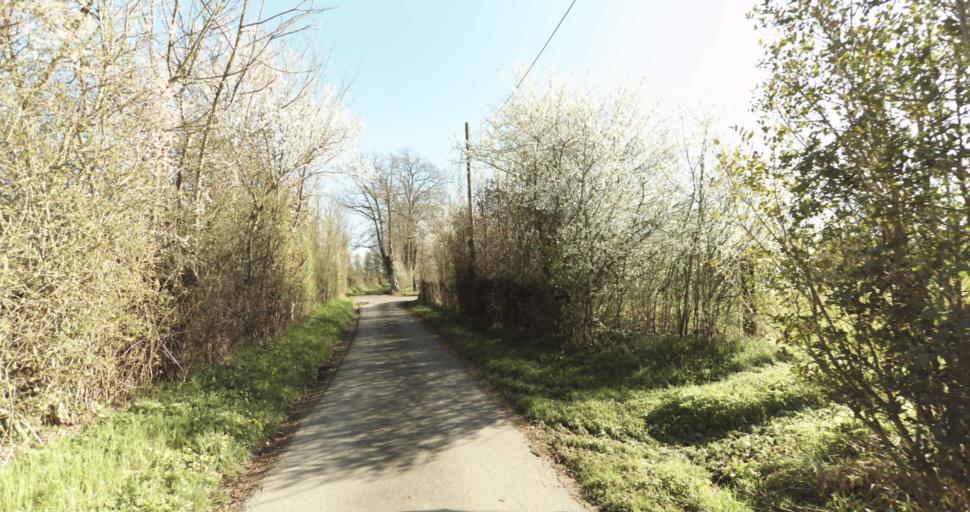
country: FR
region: Lower Normandy
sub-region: Departement du Calvados
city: Saint-Pierre-sur-Dives
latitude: 49.0375
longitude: 0.0580
